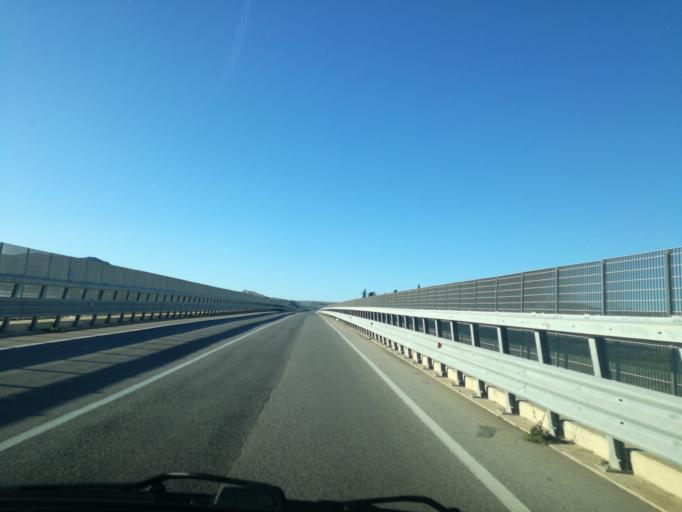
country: IT
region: Sicily
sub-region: Provincia di Caltanissetta
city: Butera
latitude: 37.1365
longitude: 14.1155
